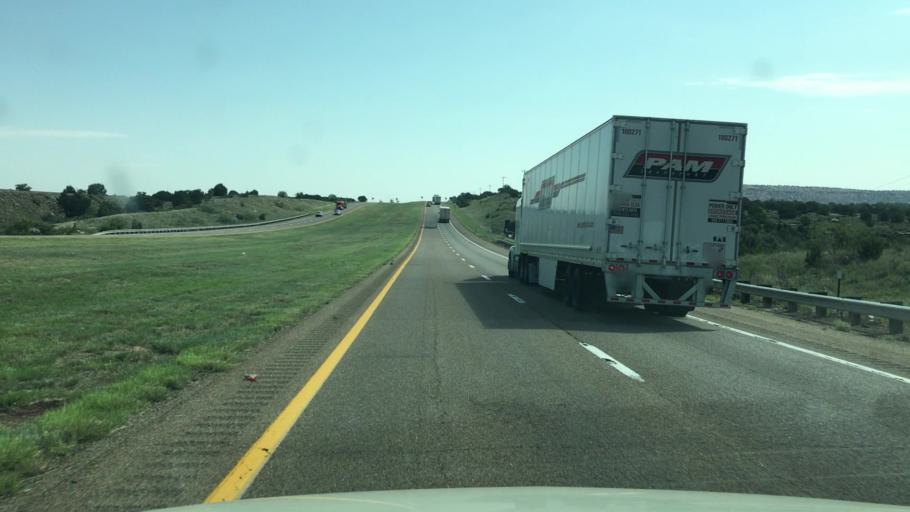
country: US
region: New Mexico
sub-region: Guadalupe County
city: Santa Rosa
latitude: 35.0188
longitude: -104.4373
